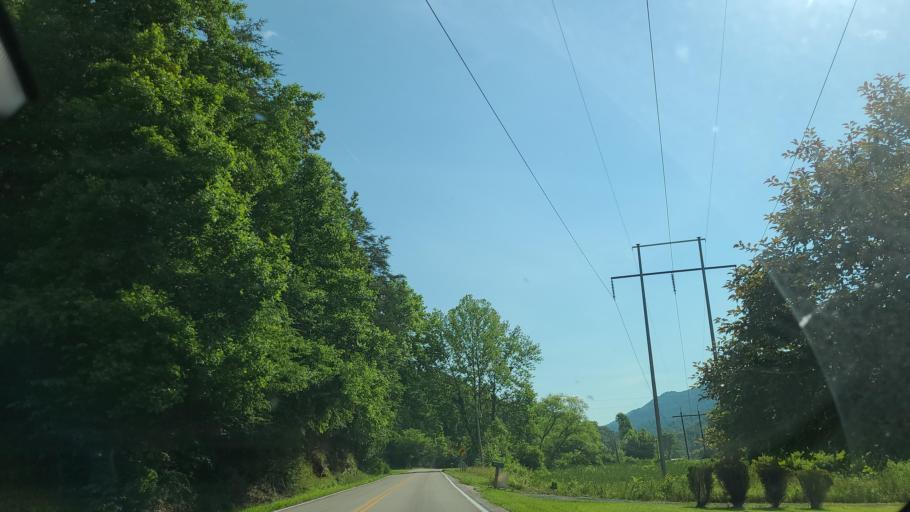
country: US
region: Kentucky
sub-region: Bell County
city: Pineville
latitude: 36.7049
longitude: -83.8411
